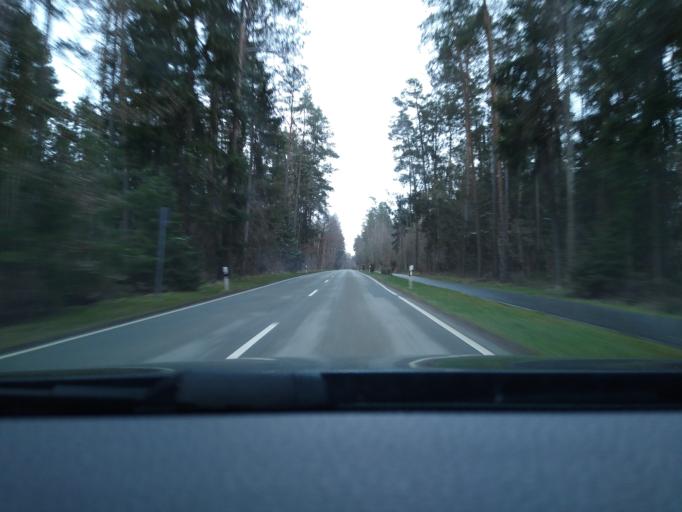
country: DE
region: Bavaria
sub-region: Regierungsbezirk Mittelfranken
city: Seukendorf
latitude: 49.4615
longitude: 10.9108
